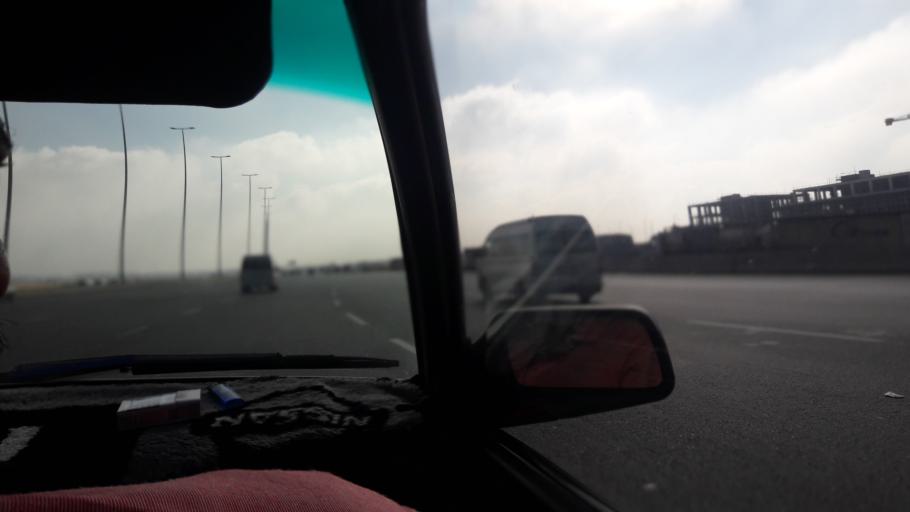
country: EG
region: Eastern Province
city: Bilbays
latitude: 30.2086
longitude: 31.6732
